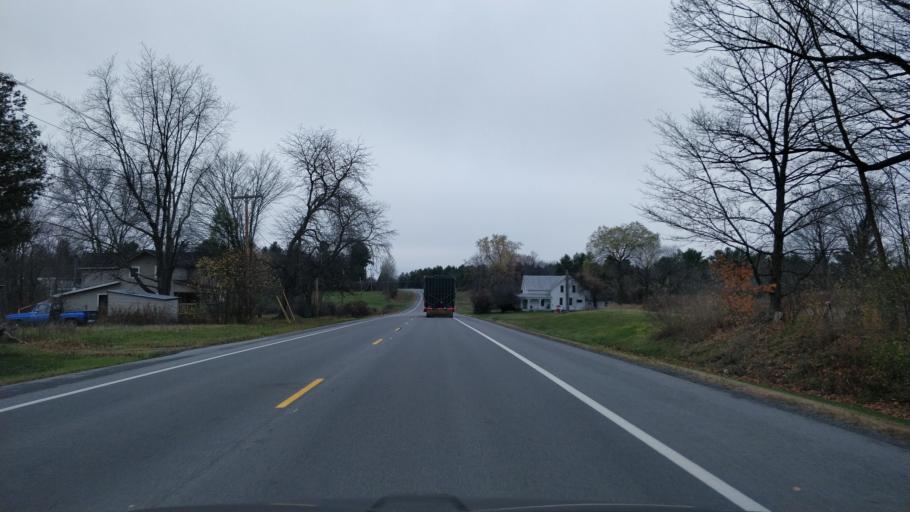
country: CA
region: Ontario
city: Brockville
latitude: 44.6122
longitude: -75.6036
